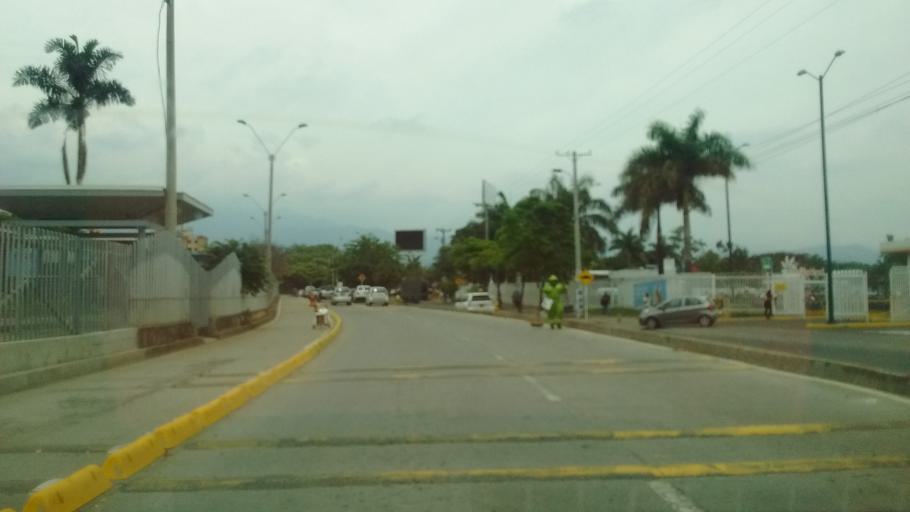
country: CO
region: Valle del Cauca
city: Cali
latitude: 3.3669
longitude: -76.5283
